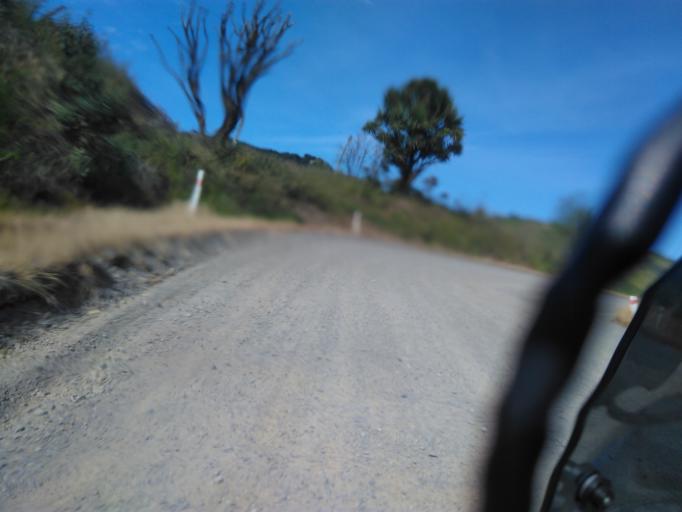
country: NZ
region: Hawke's Bay
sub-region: Wairoa District
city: Wairoa
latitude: -38.8706
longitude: 177.2074
